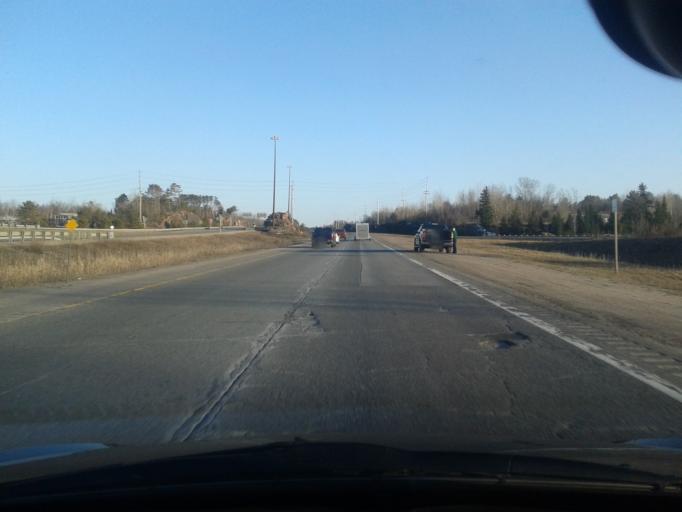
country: CA
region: Ontario
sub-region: Nipissing District
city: North Bay
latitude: 46.3049
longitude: -79.4322
